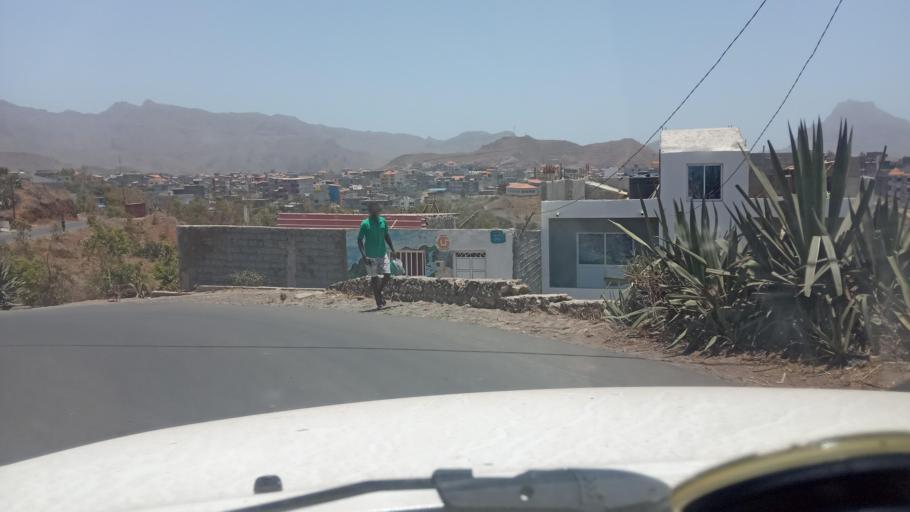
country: CV
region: Santa Catarina
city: Assomada
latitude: 15.1019
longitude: -23.6629
